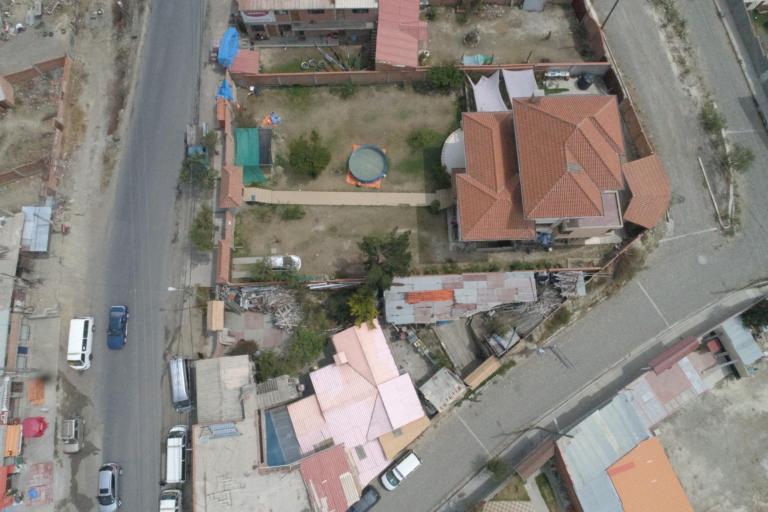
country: BO
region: La Paz
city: La Paz
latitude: -16.6003
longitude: -68.0703
